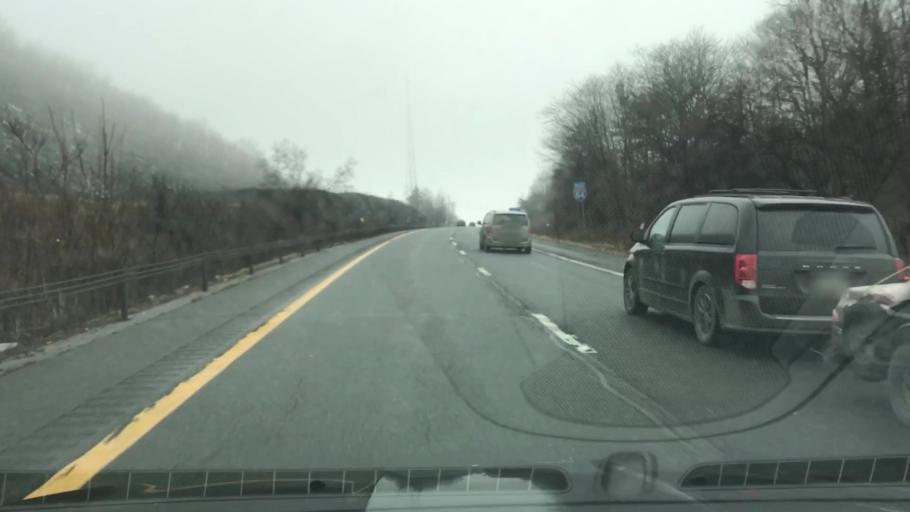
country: US
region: New York
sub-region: Orange County
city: Port Jervis
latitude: 41.3735
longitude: -74.6219
